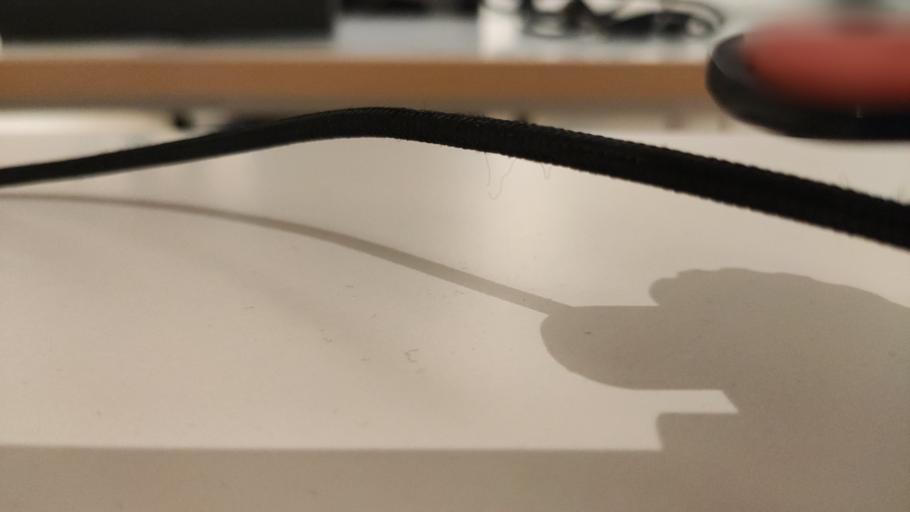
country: RU
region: Moskovskaya
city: Dorokhovo
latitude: 55.3731
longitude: 36.4091
